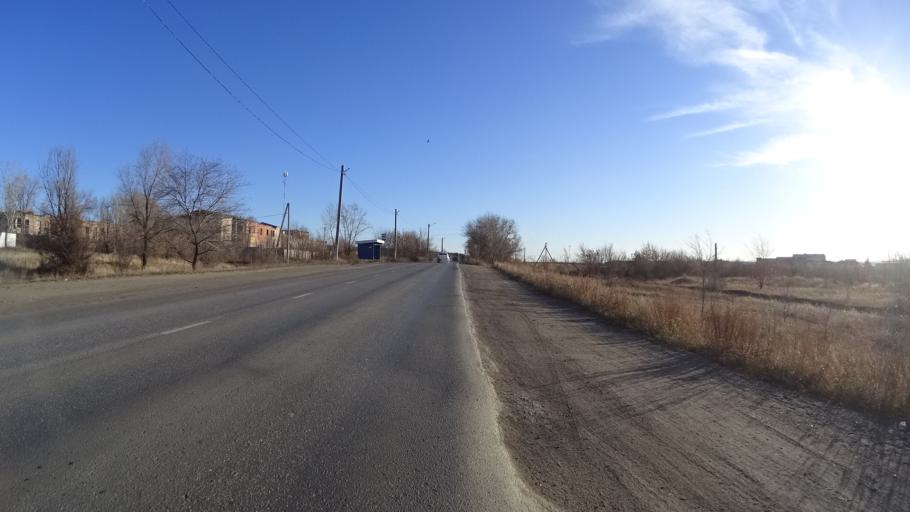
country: RU
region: Chelyabinsk
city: Troitsk
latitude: 54.0821
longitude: 61.5965
